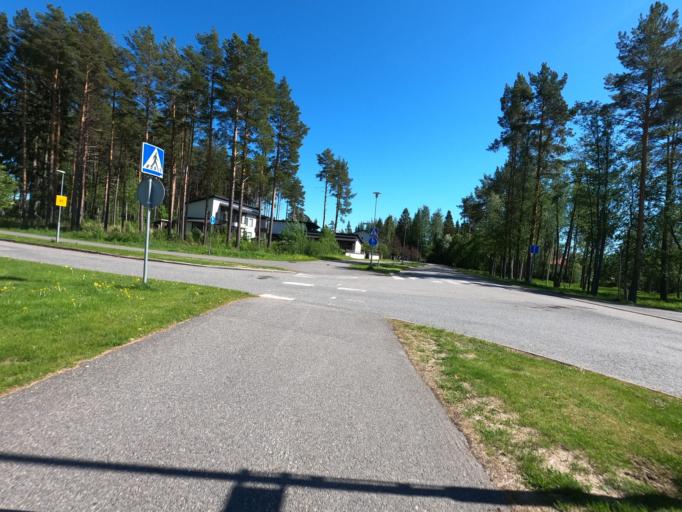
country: FI
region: North Karelia
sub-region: Joensuu
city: Joensuu
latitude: 62.5768
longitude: 29.7677
